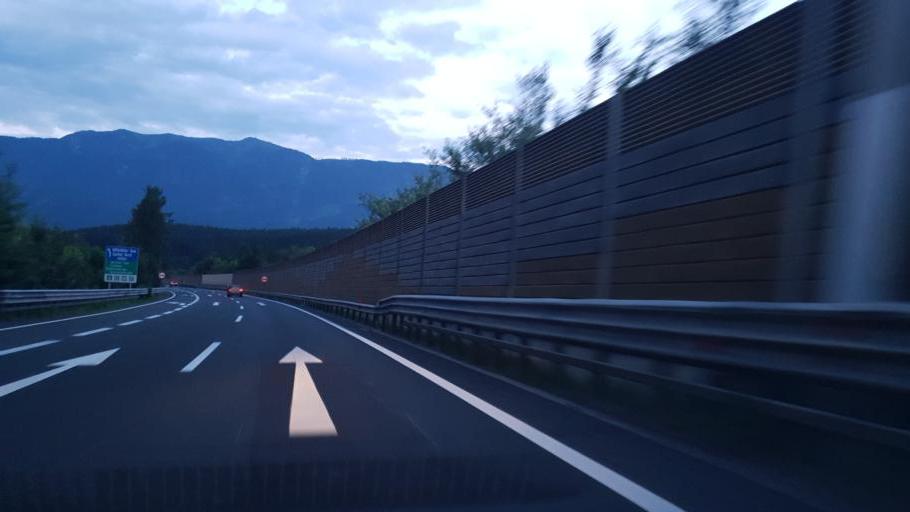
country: AT
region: Carinthia
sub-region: Politischer Bezirk Spittal an der Drau
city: Seeboden
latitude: 46.8294
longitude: 13.4852
